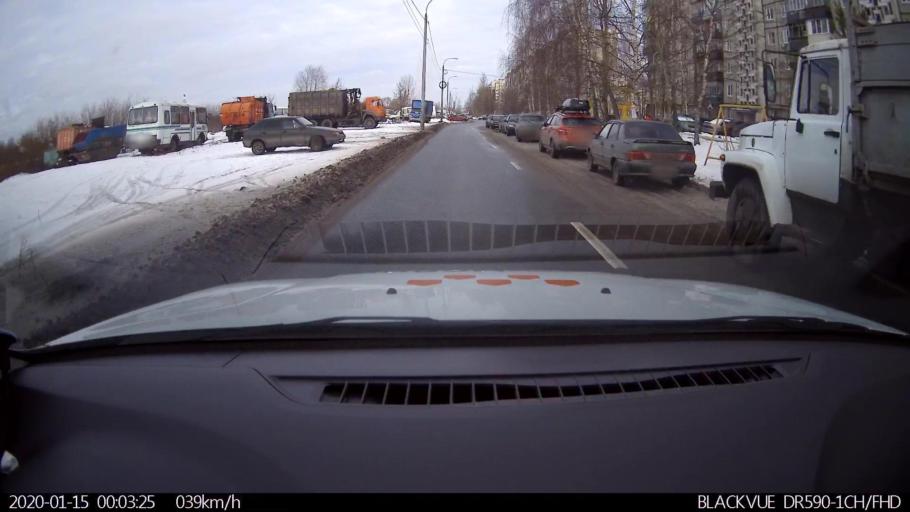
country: RU
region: Nizjnij Novgorod
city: Gorbatovka
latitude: 56.2717
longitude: 43.8778
